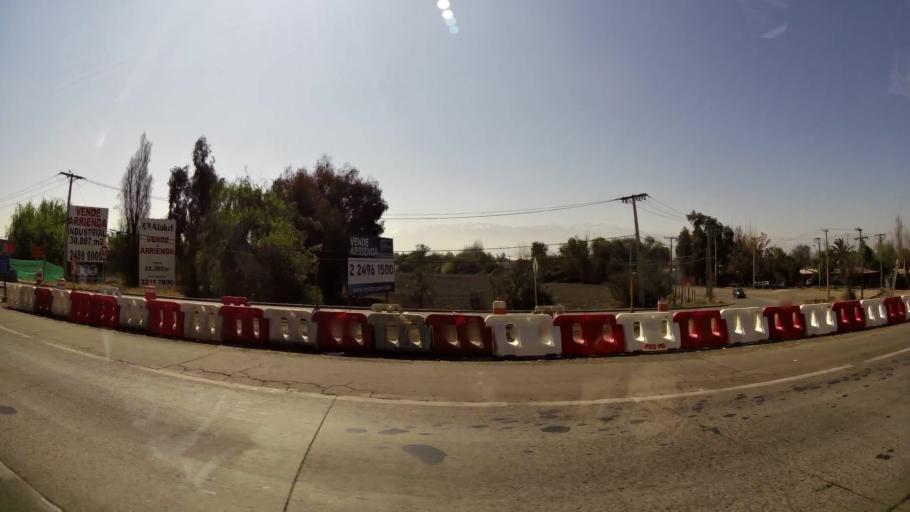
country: CL
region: Santiago Metropolitan
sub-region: Provincia de Chacabuco
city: Chicureo Abajo
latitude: -33.2699
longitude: -70.7433
